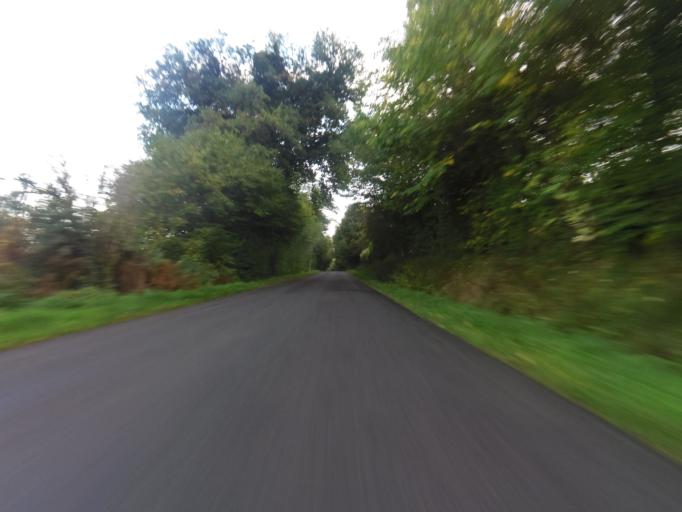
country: FR
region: Lower Normandy
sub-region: Departement de l'Orne
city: Vimoutiers
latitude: 48.9524
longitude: 0.2646
